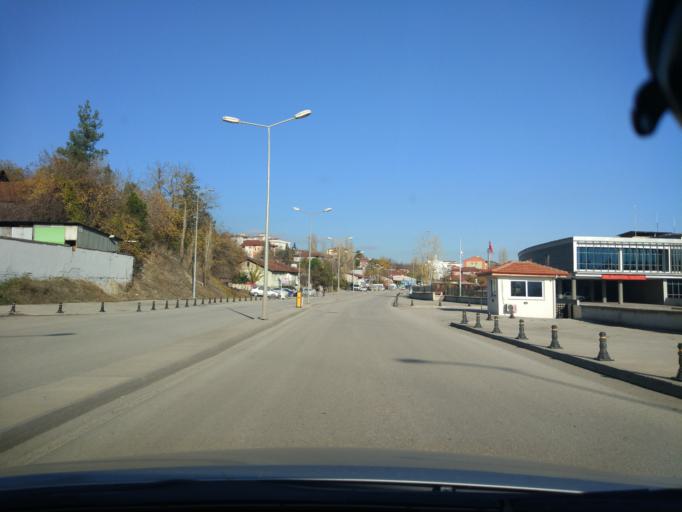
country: TR
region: Karabuk
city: Karabuk
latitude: 41.2052
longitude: 32.6329
